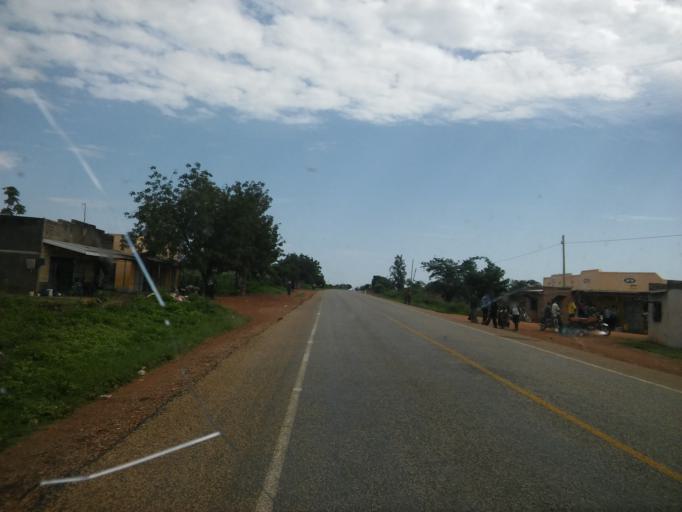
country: UG
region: Eastern Region
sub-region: Bukedea District
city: Bukedea
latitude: 1.2670
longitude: 34.0865
